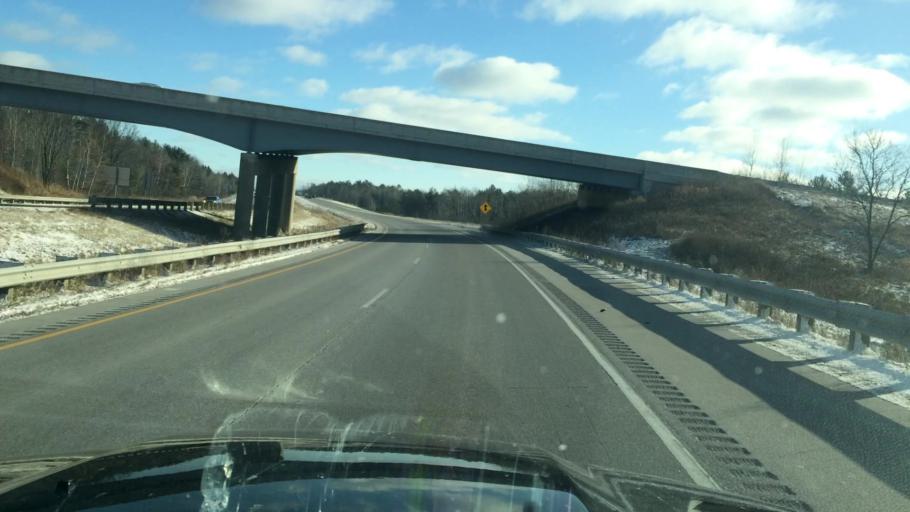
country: US
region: Wisconsin
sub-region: Portage County
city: Stevens Point
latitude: 44.5485
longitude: -89.5774
